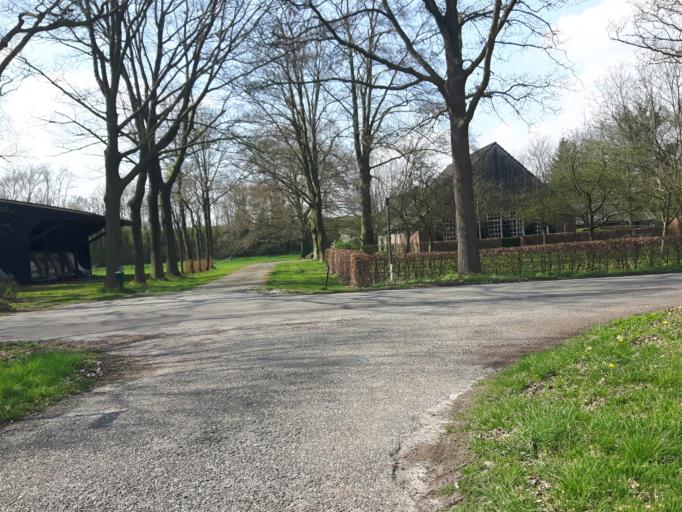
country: NL
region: Overijssel
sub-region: Gemeente Hengelo
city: Hengelo
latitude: 52.2082
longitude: 6.8273
